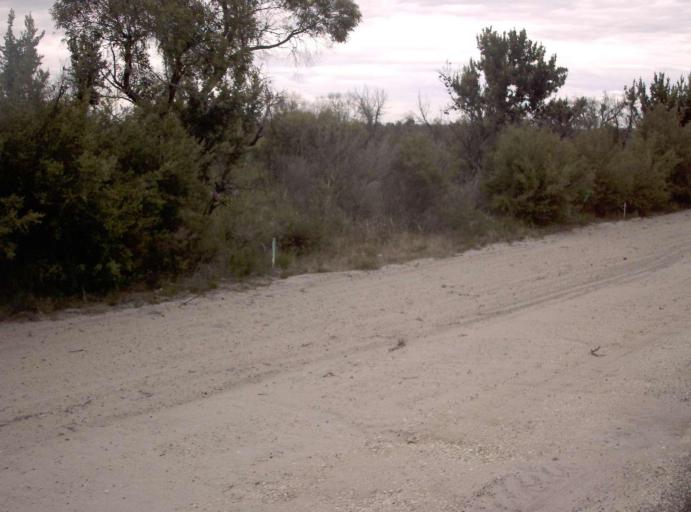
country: AU
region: Victoria
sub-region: East Gippsland
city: Bairnsdale
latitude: -38.1229
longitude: 147.4522
